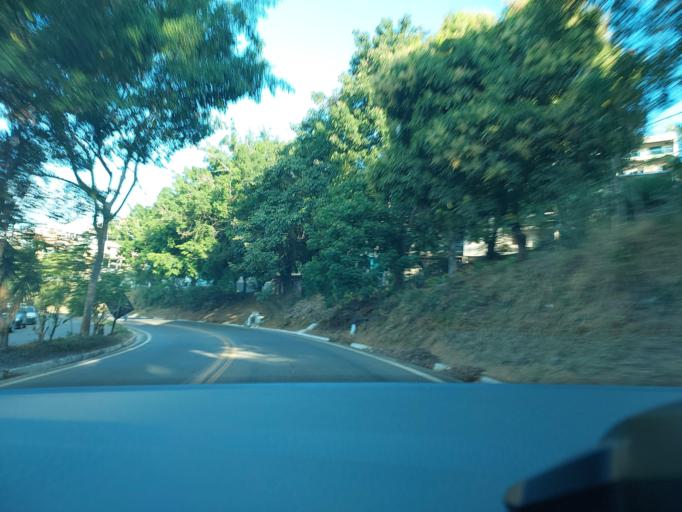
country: BR
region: Minas Gerais
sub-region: Muriae
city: Muriae
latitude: -21.1276
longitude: -42.4030
